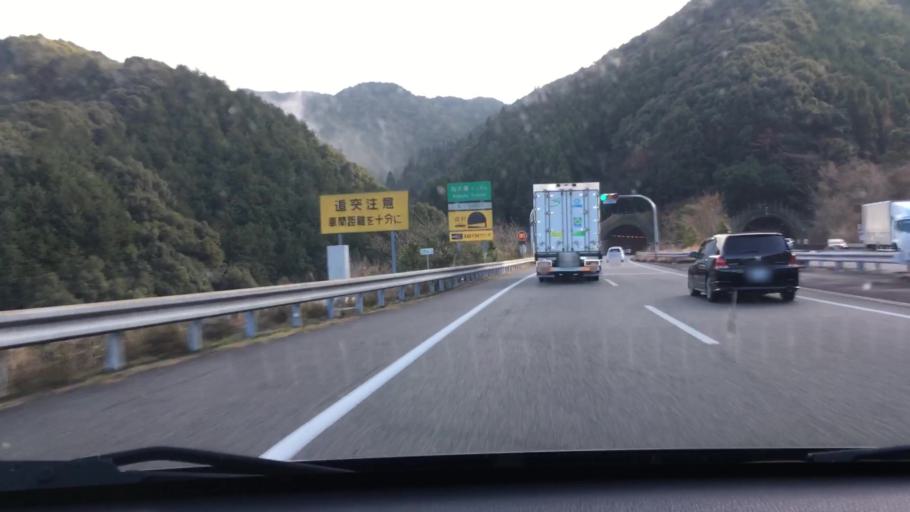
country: JP
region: Kumamoto
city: Hitoyoshi
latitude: 32.1357
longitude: 130.8036
